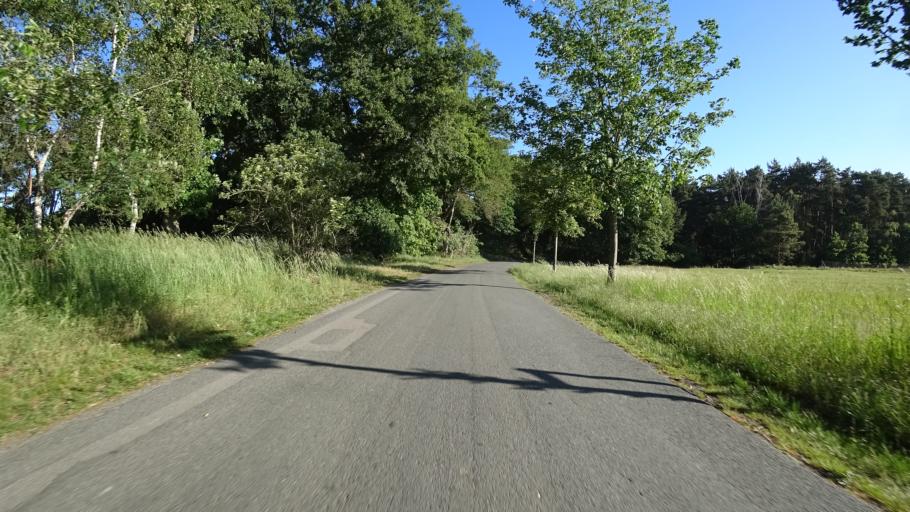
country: DE
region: North Rhine-Westphalia
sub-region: Regierungsbezirk Detmold
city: Rheda-Wiedenbruck
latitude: 51.8768
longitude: 8.3155
